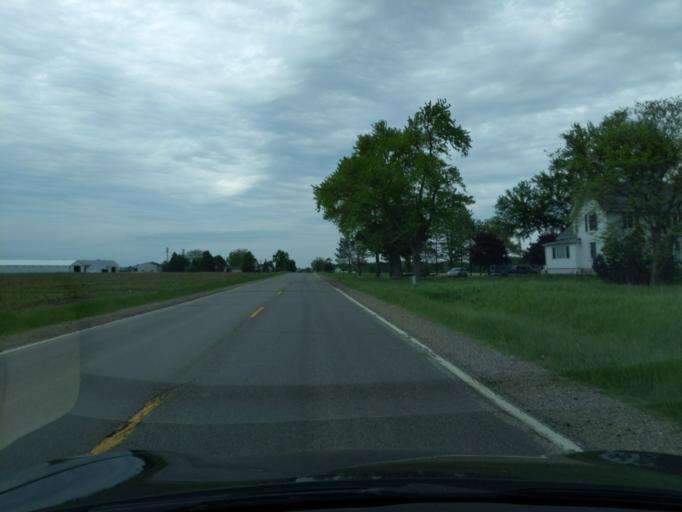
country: US
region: Michigan
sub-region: Ingham County
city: Mason
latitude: 42.6307
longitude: -84.3639
